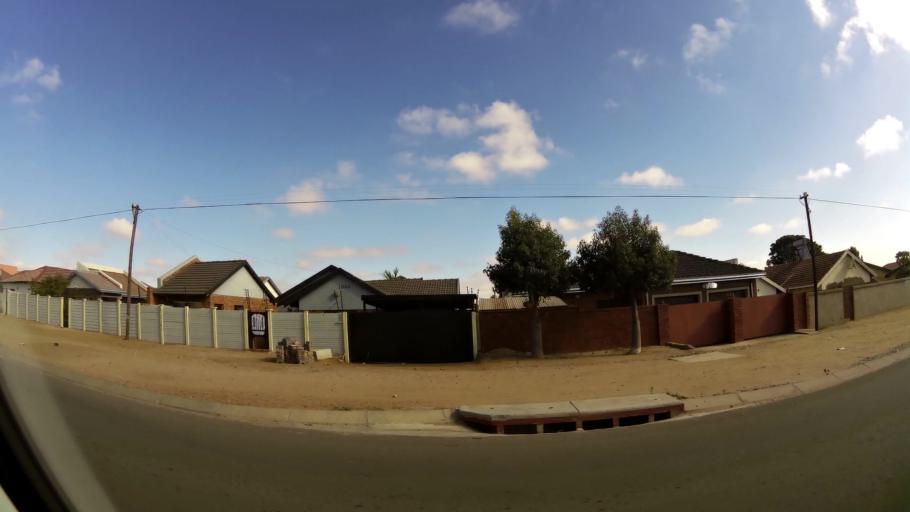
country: ZA
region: Limpopo
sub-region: Capricorn District Municipality
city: Polokwane
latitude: -23.8560
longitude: 29.3764
